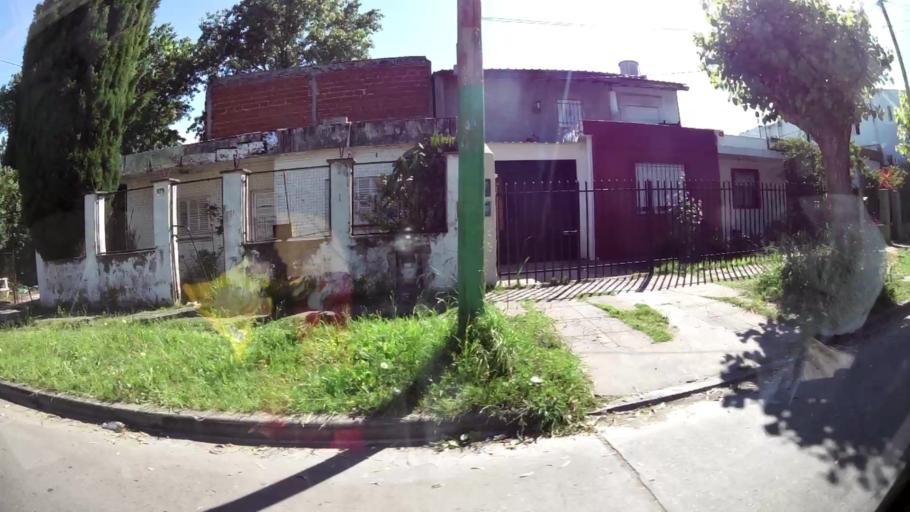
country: AR
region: Buenos Aires
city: Ituzaingo
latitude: -34.6218
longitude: -58.6578
